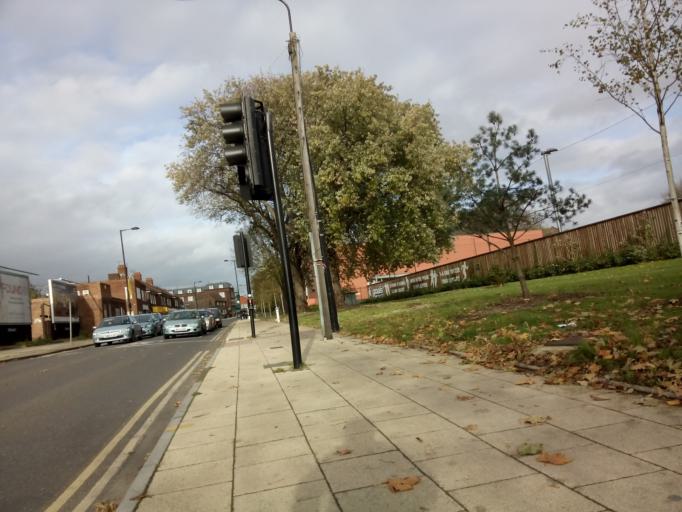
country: GB
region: England
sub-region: Suffolk
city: Ipswich
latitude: 52.0541
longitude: 1.1628
